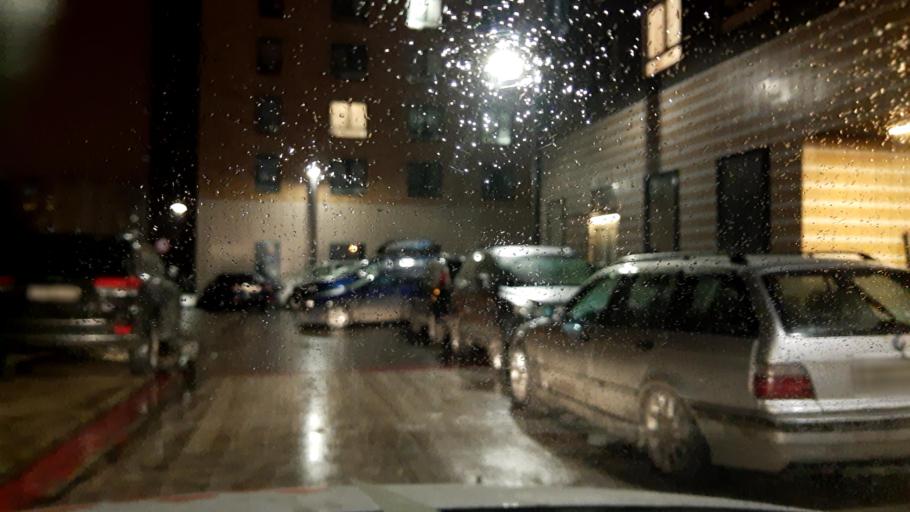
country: RU
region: Moscow
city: Annino
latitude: 55.5556
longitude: 37.5574
